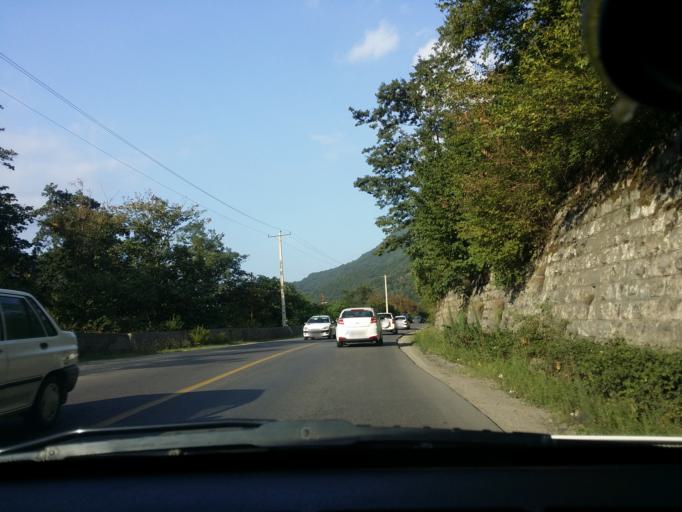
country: IR
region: Mazandaran
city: Chalus
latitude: 36.5501
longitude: 51.3657
